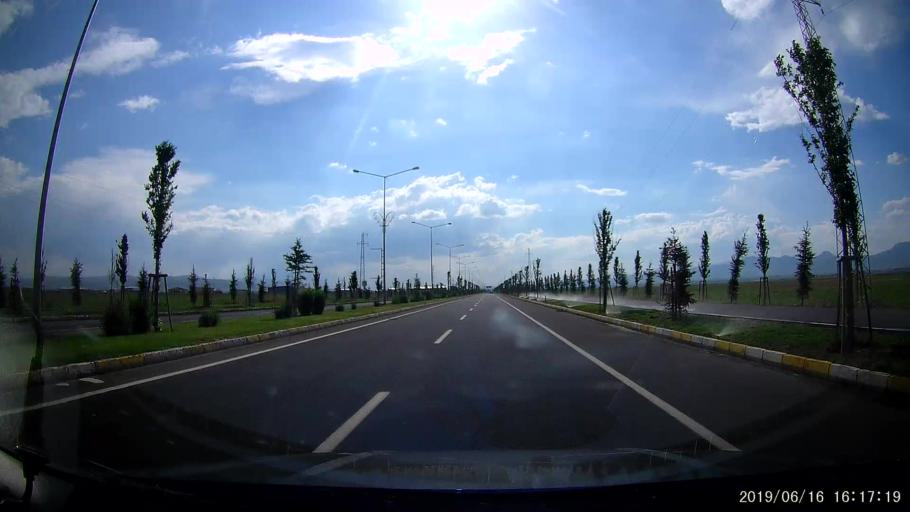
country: TR
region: Erzurum
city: Ilica
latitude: 39.9638
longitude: 41.1897
